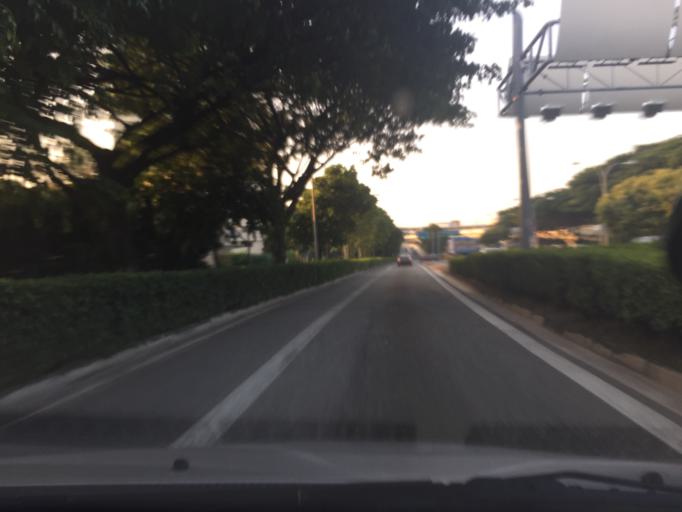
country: SG
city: Singapore
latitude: 1.3169
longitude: 103.8744
